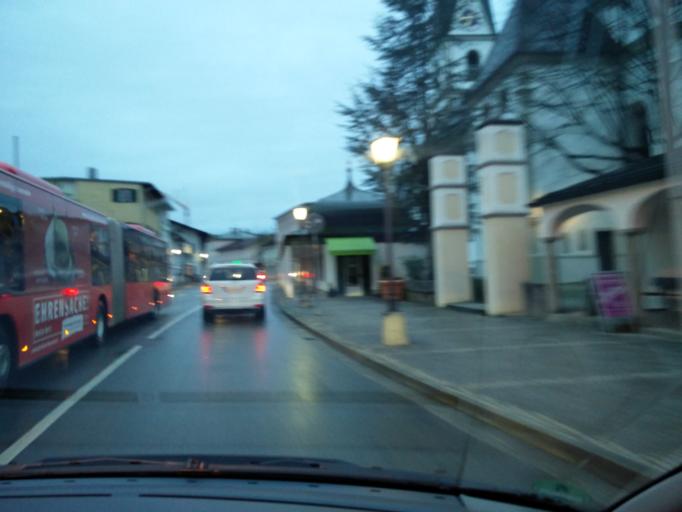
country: DE
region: Bavaria
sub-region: Upper Bavaria
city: Prien am Chiemsee
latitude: 47.8555
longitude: 12.3445
